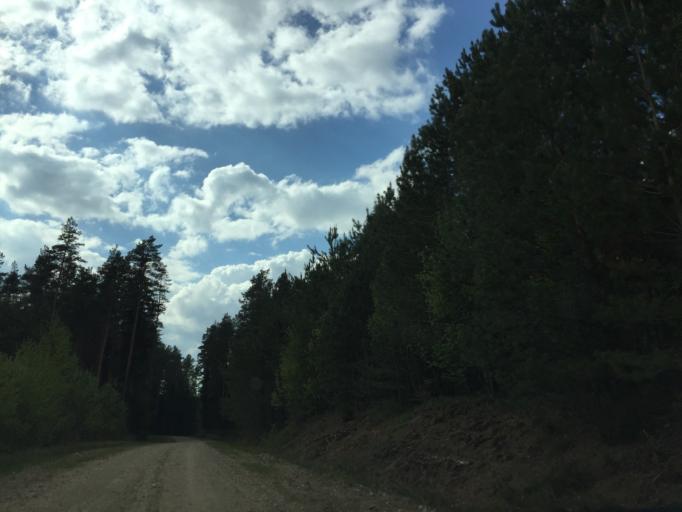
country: LV
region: Sigulda
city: Sigulda
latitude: 57.2955
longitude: 24.8600
